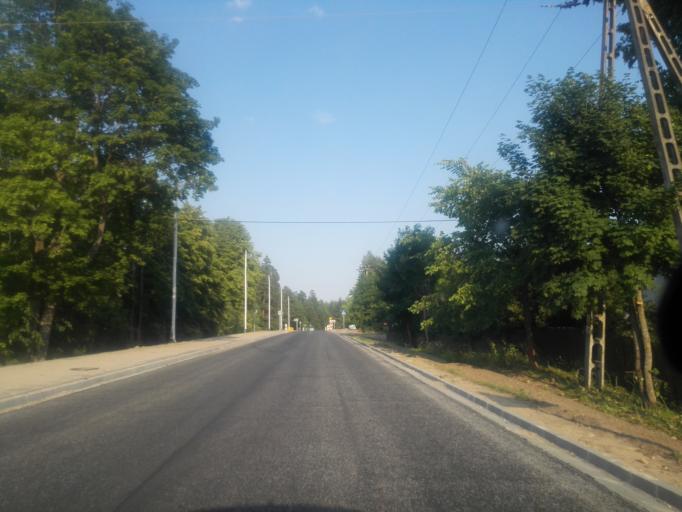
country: PL
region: Podlasie
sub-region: Suwalki
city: Suwalki
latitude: 54.0836
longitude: 23.0107
